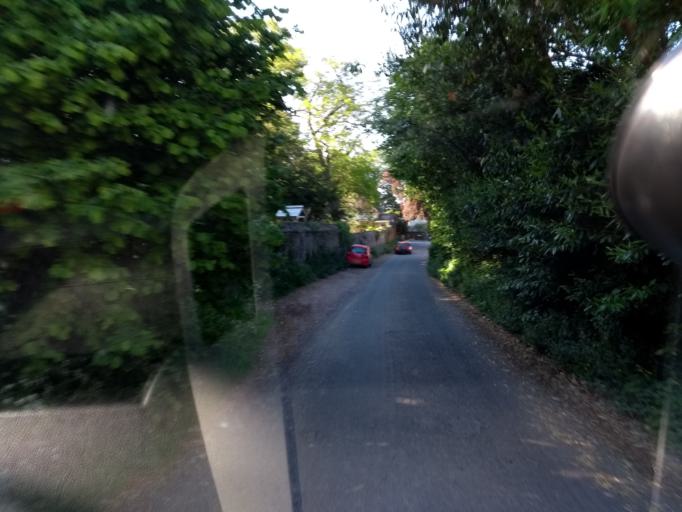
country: GB
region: England
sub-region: Somerset
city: Creech Saint Michael
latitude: 51.0504
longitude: -3.0545
